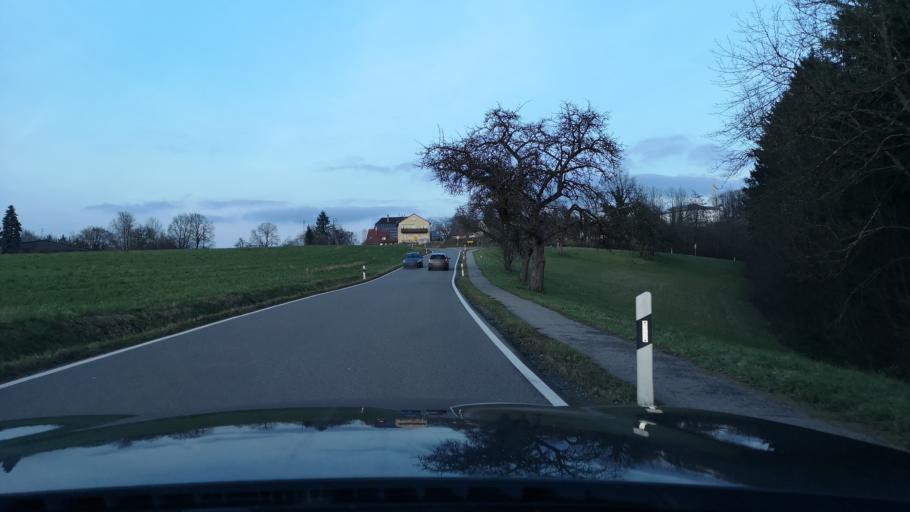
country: DE
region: Baden-Wuerttemberg
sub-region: Regierungsbezirk Stuttgart
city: Althutte
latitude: 48.9110
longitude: 9.5466
